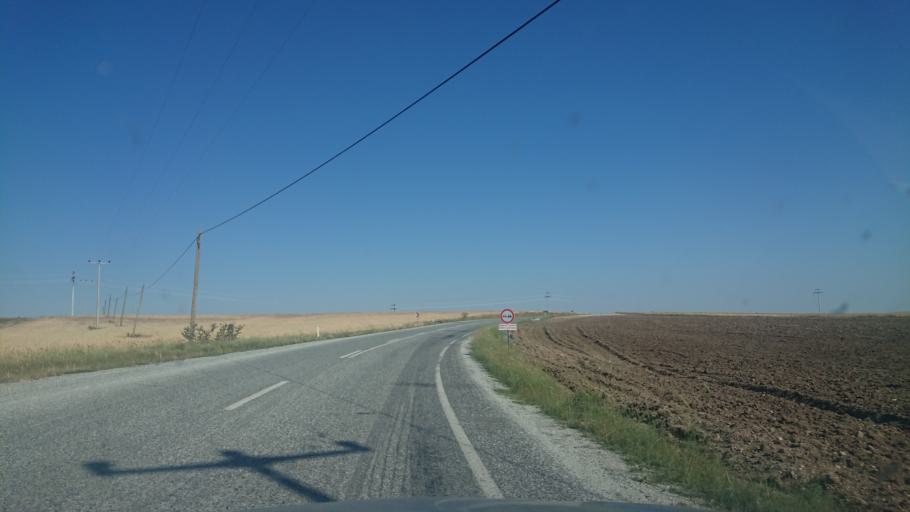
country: TR
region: Aksaray
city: Agacoren
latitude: 38.8693
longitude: 33.8858
